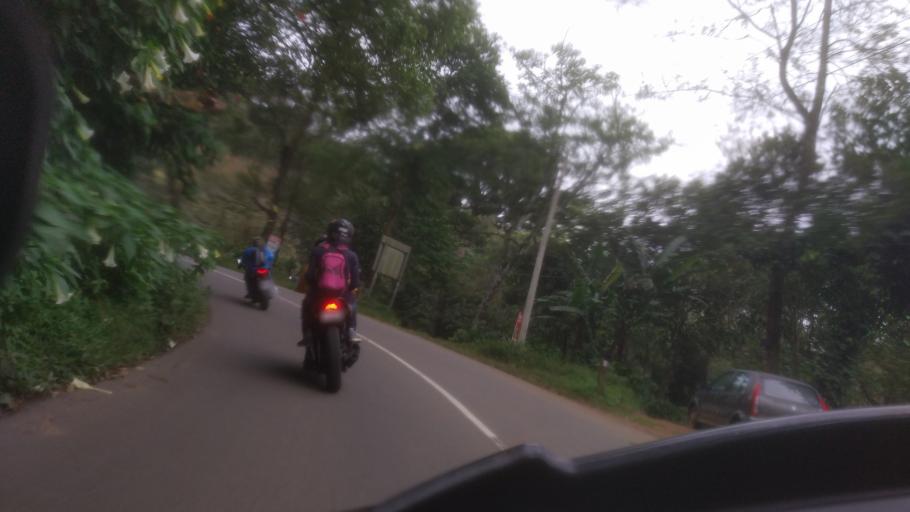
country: IN
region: Tamil Nadu
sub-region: Theni
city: Kombai
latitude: 9.8936
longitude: 77.1584
